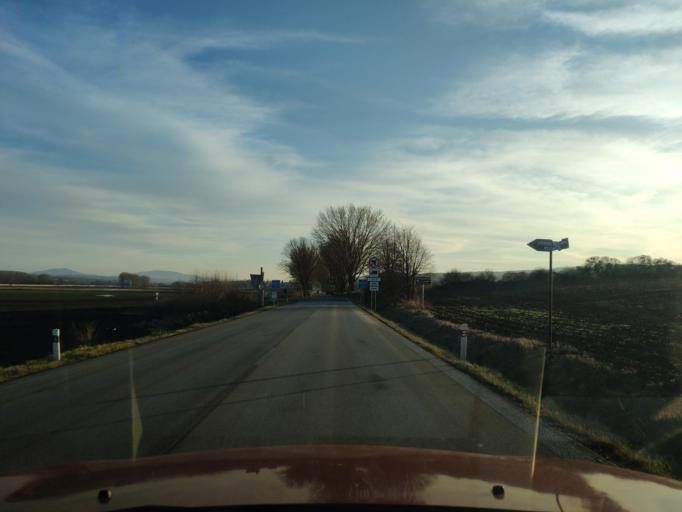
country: SK
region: Kosicky
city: Kosice
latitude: 48.8166
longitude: 21.2996
